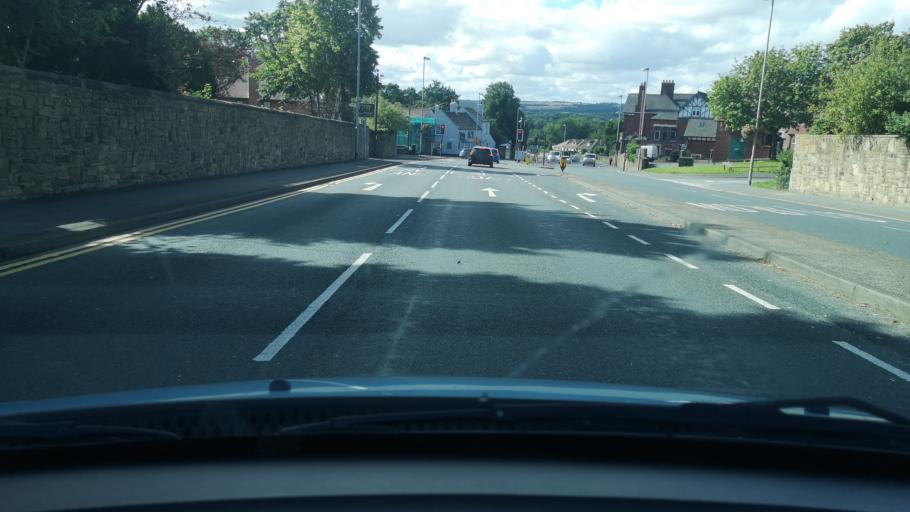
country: GB
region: England
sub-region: City and Borough of Wakefield
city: Walton
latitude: 53.6555
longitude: -1.4866
